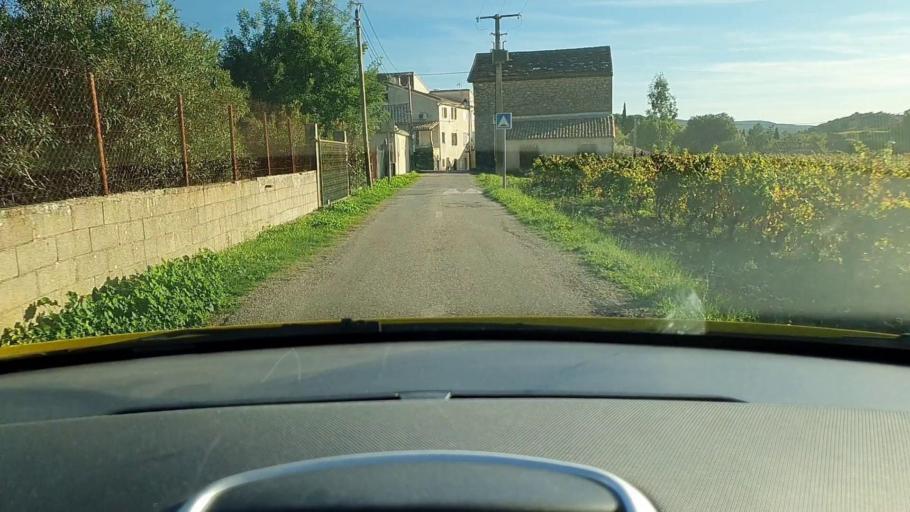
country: FR
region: Languedoc-Roussillon
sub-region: Departement du Gard
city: Saint-Hippolyte-du-Fort
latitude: 43.9578
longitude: 3.8071
